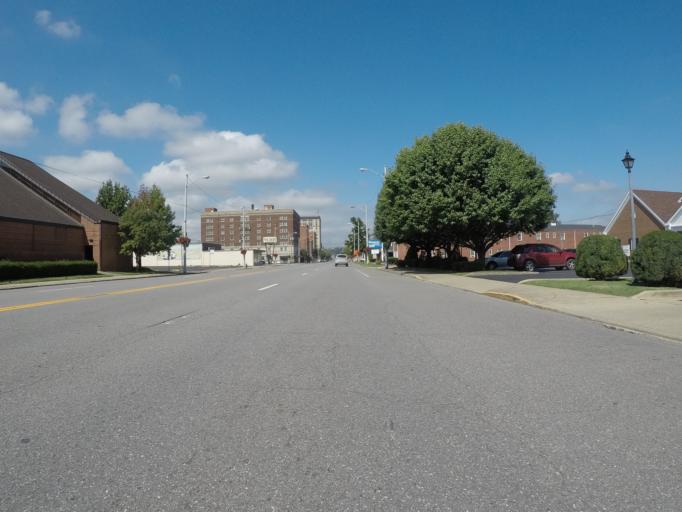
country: US
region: Kentucky
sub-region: Boyd County
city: Ashland
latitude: 38.4768
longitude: -82.6357
